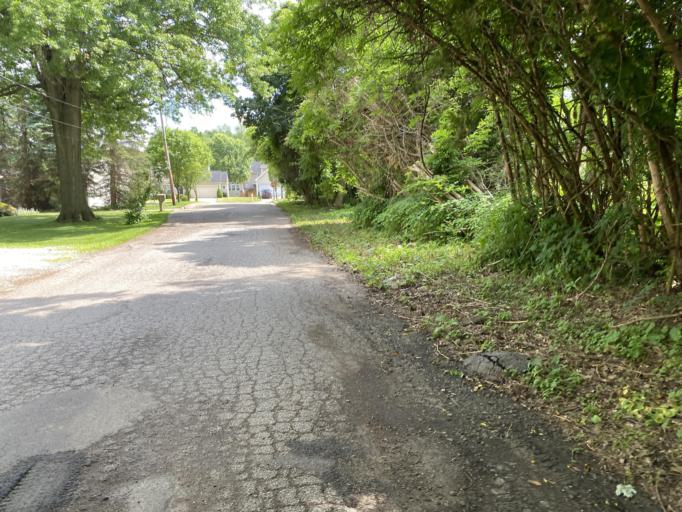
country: US
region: Ohio
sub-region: Summit County
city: Fairlawn
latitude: 41.1039
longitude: -81.5830
